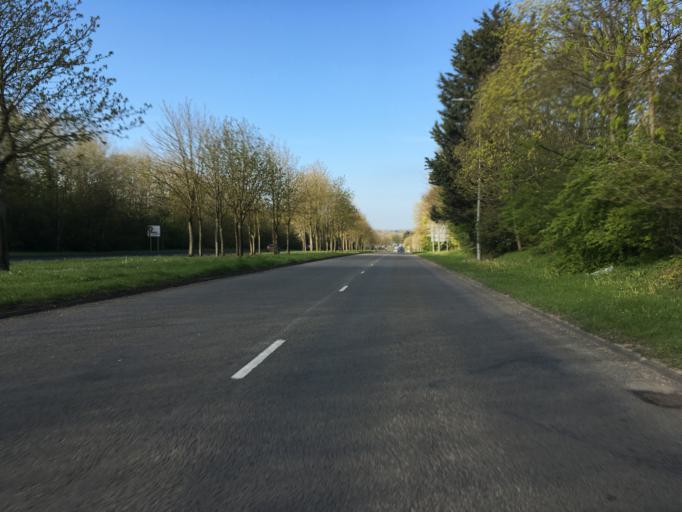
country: GB
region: England
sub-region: Milton Keynes
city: Bradwell
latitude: 52.0567
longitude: -0.7761
